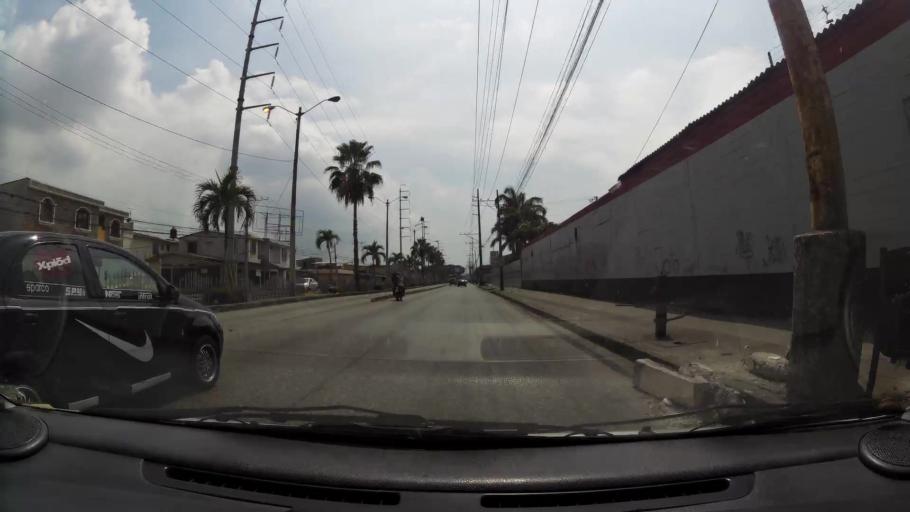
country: EC
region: Guayas
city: Guayaquil
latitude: -2.2351
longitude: -79.8907
